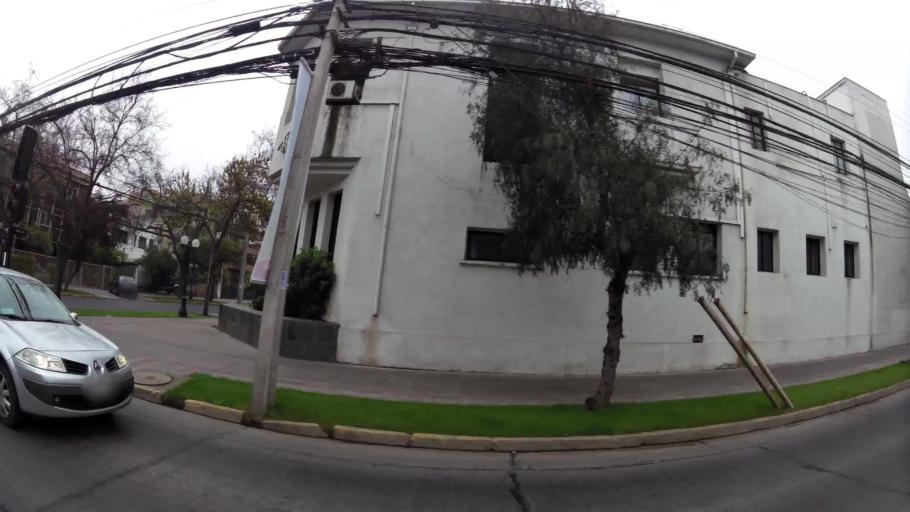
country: CL
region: Santiago Metropolitan
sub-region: Provincia de Santiago
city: Santiago
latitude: -33.4387
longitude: -70.6182
